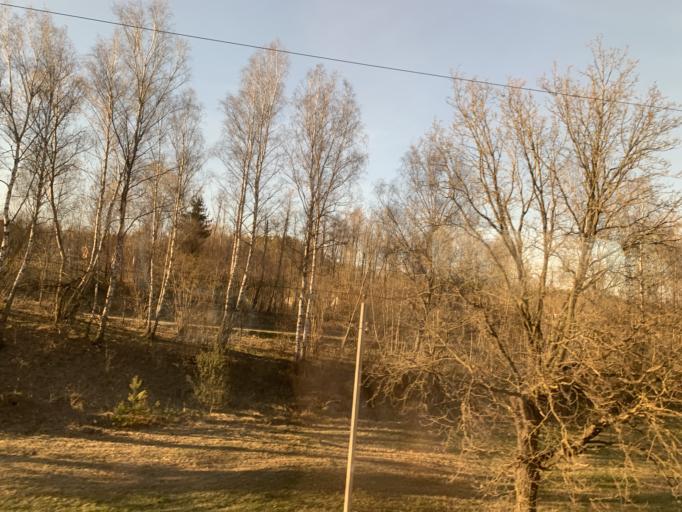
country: BY
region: Minsk
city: Pyatryshki
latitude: 54.1000
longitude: 27.1668
